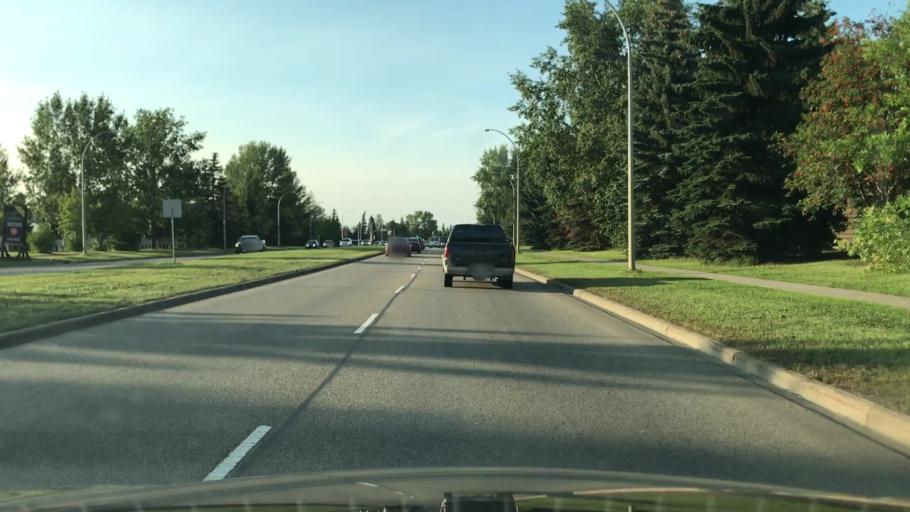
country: CA
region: Alberta
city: Beaumont
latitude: 53.4431
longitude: -113.4186
